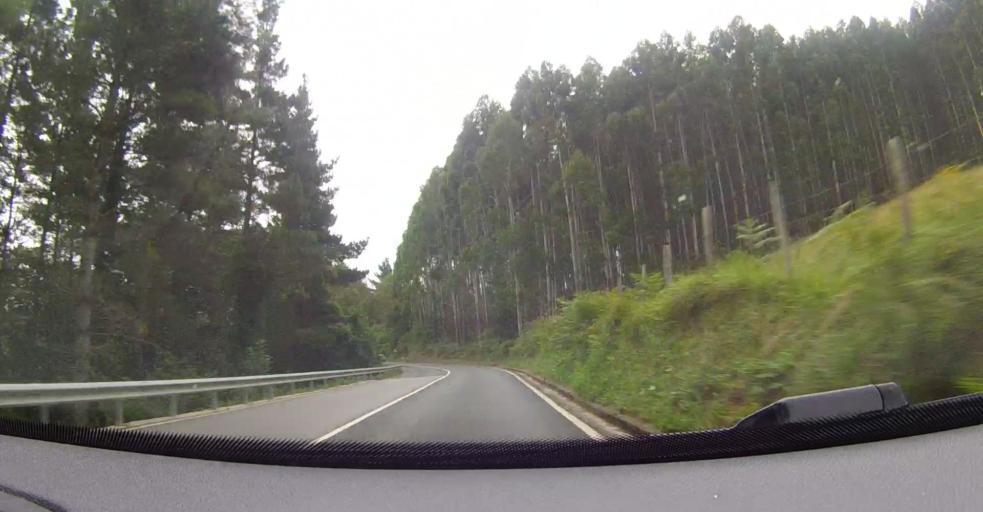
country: ES
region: Basque Country
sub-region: Bizkaia
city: Balmaseda
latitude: 43.2300
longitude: -3.1966
